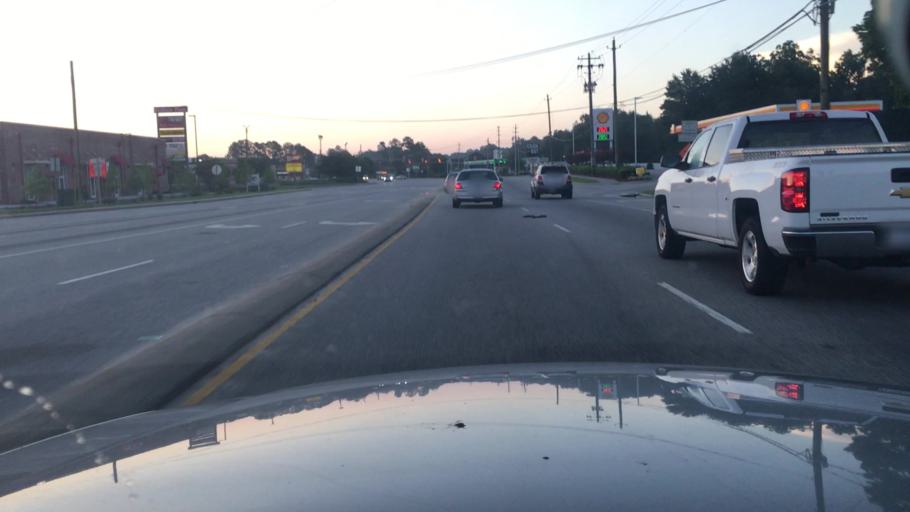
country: US
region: North Carolina
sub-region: Cumberland County
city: Fort Bragg
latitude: 35.0611
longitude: -79.0148
